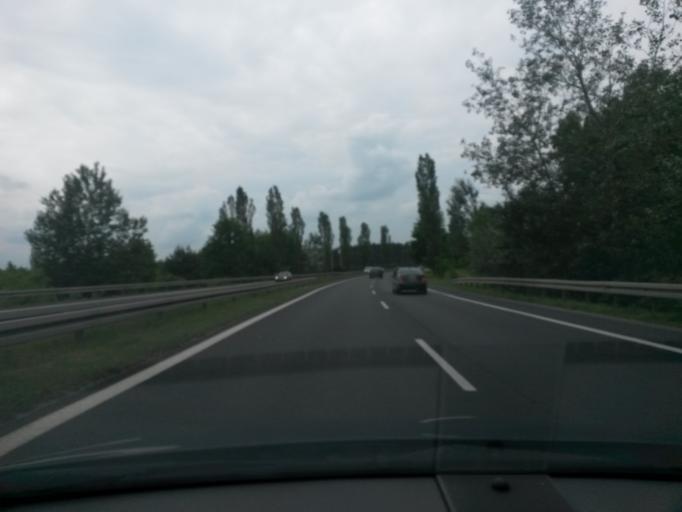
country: PL
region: Masovian Voivodeship
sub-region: Powiat pruszkowski
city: Nadarzyn
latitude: 52.0860
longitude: 20.8071
